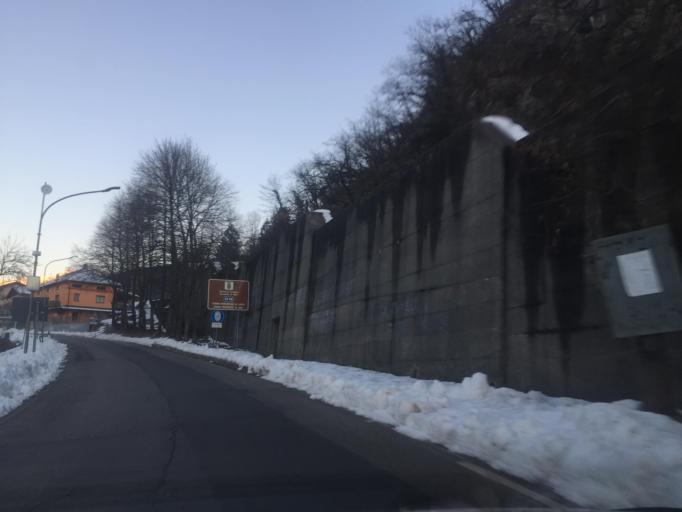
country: IT
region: Friuli Venezia Giulia
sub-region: Provincia di Udine
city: Villa Santina
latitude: 46.4180
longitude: 12.9204
